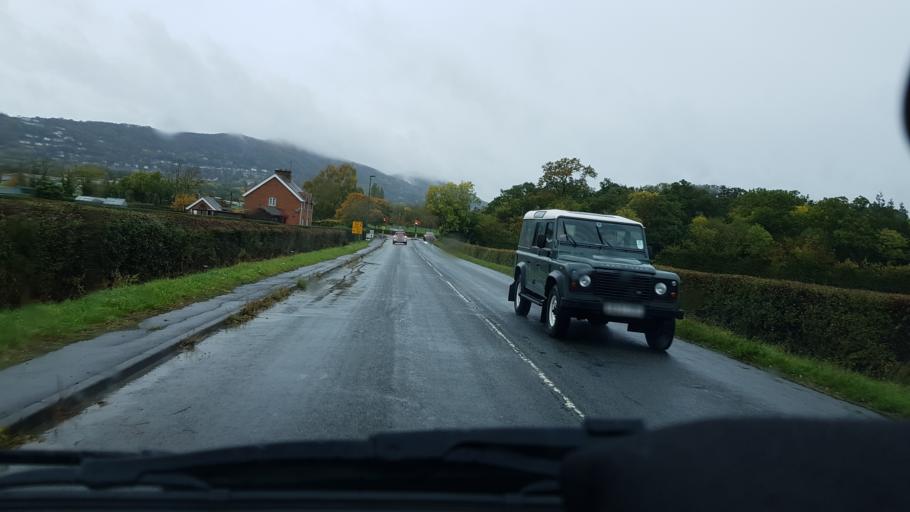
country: GB
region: England
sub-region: Worcestershire
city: Great Malvern
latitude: 52.0787
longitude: -2.3066
